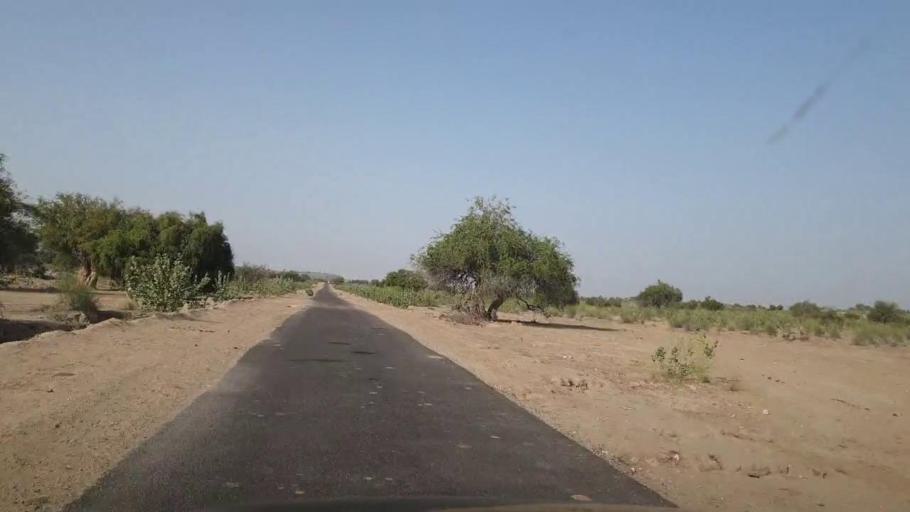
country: PK
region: Sindh
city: Islamkot
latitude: 25.1503
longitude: 70.5203
